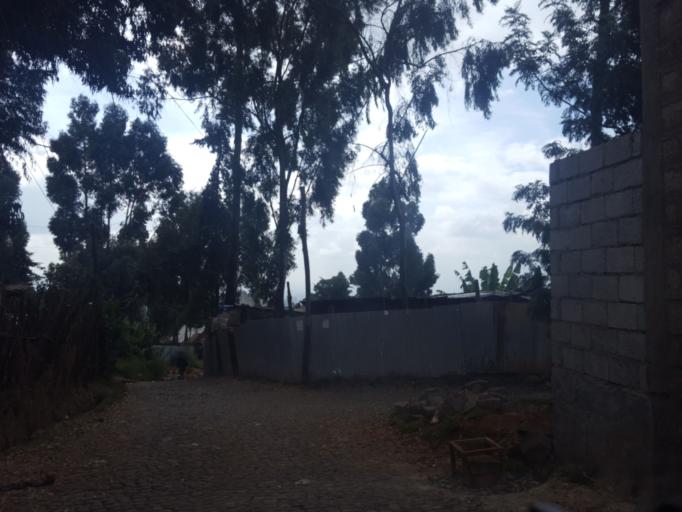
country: ET
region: Adis Abeba
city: Addis Ababa
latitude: 9.0663
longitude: 38.7455
